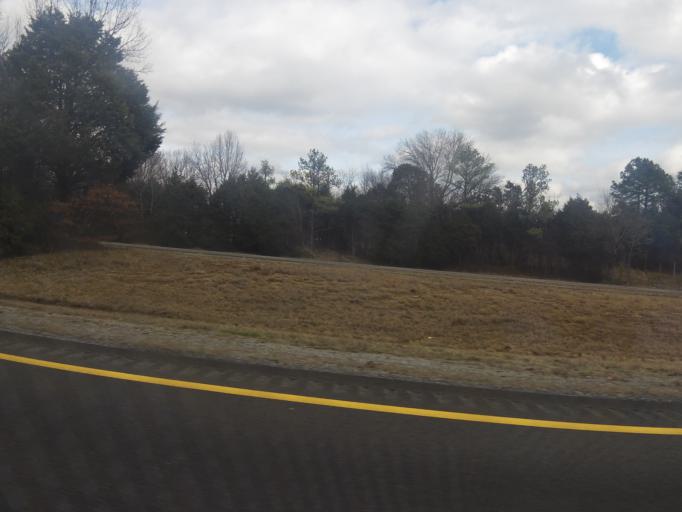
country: US
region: Tennessee
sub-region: Rutherford County
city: Plainview
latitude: 35.7587
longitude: -86.3509
